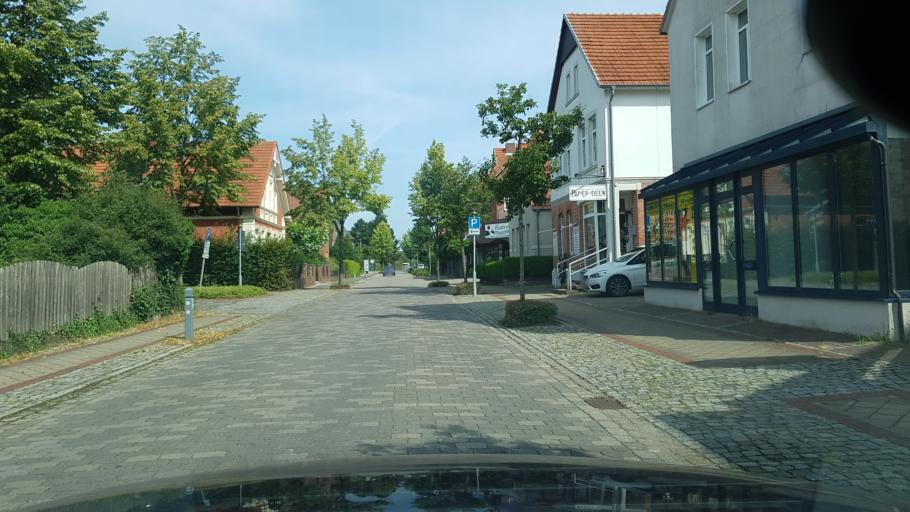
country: DE
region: Lower Saxony
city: Sulingen
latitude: 52.6831
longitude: 8.8088
